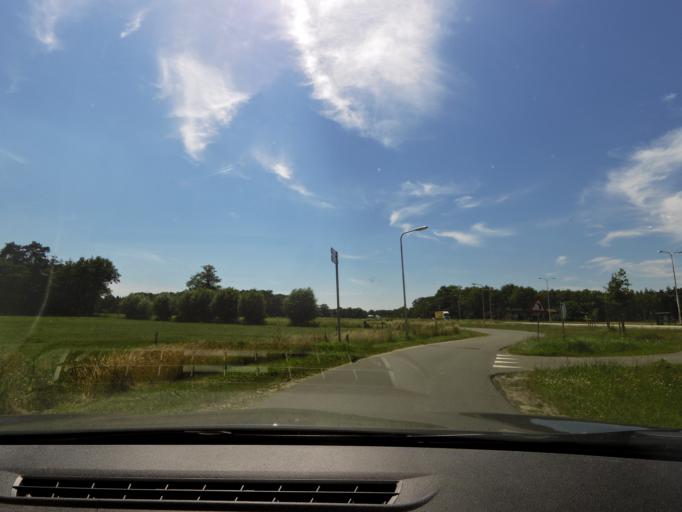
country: NL
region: Overijssel
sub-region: Gemeente Wierden
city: Wierden
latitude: 52.3333
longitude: 6.5570
